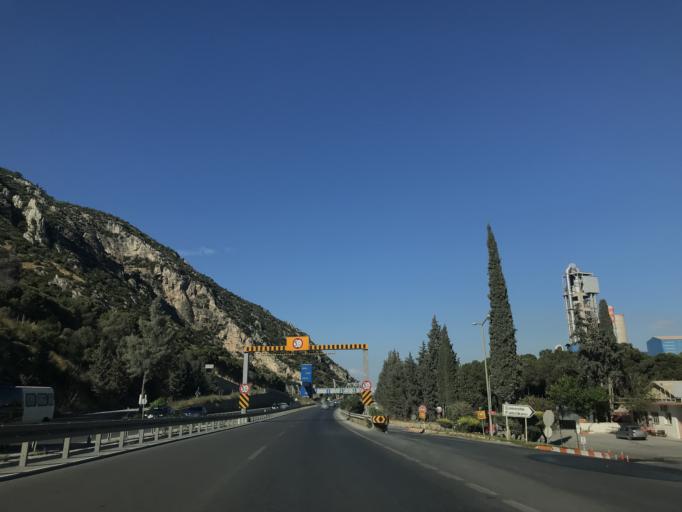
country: TR
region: Aydin
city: Soeke
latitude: 37.7715
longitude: 27.4309
